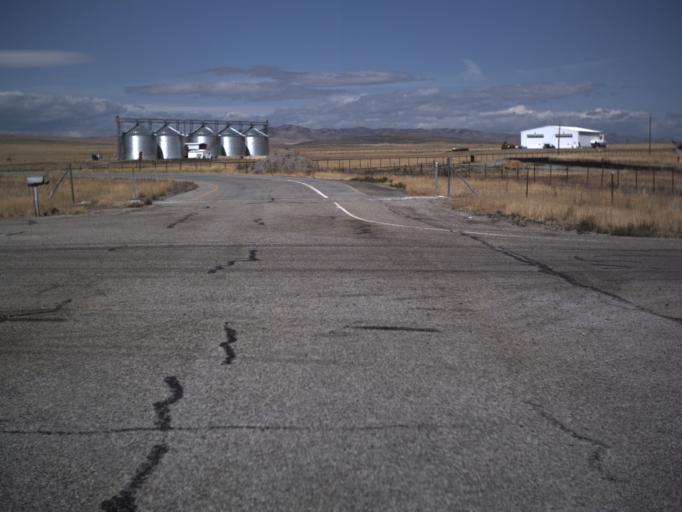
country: US
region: Utah
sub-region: Box Elder County
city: Garland
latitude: 41.8419
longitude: -112.4355
